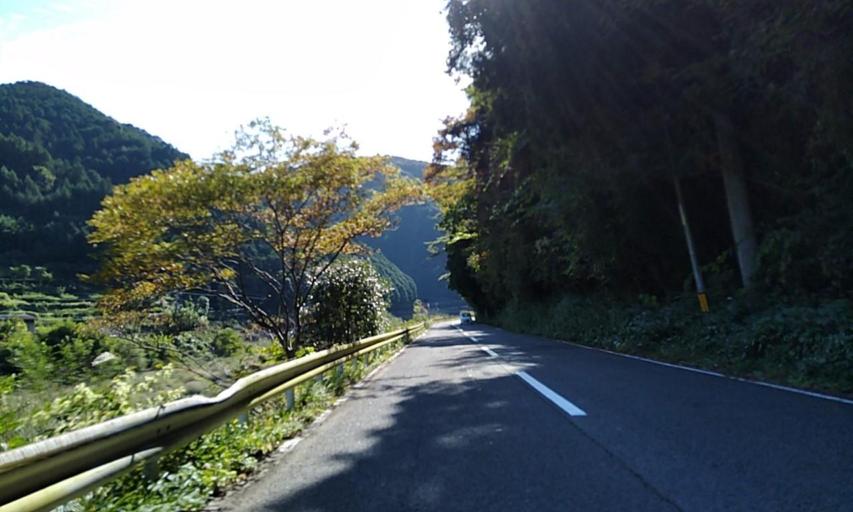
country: JP
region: Wakayama
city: Kainan
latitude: 34.0665
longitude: 135.3569
